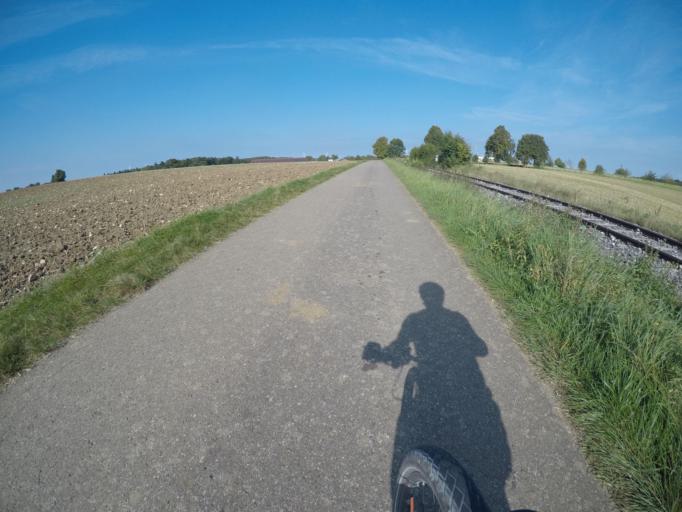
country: DE
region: Baden-Wuerttemberg
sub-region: Regierungsbezirk Stuttgart
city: Gerstetten
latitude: 48.6344
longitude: 9.9750
